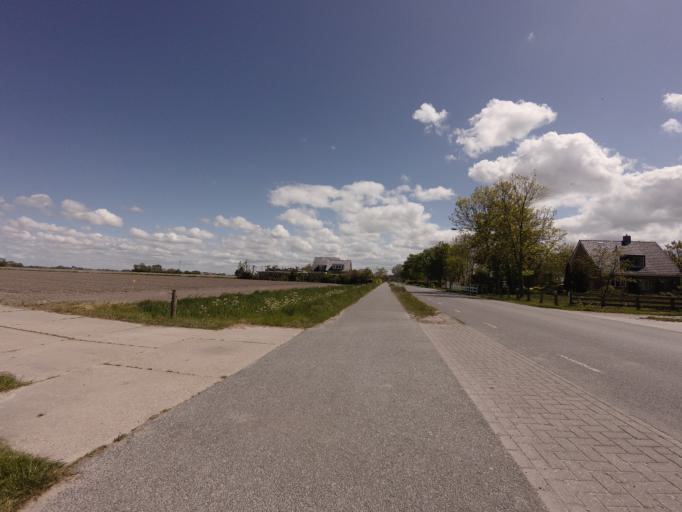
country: NL
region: Friesland
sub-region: Gemeente Harlingen
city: Harlingen
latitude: 53.1406
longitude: 5.4410
